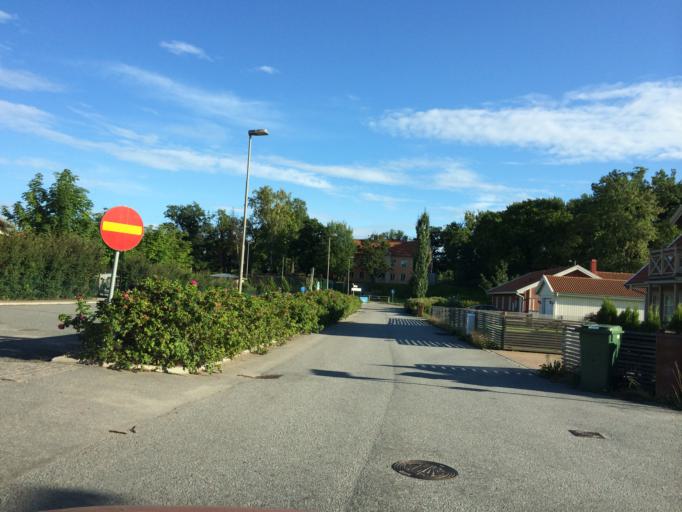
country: SE
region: Stockholm
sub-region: Huddinge Kommun
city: Segeltorp
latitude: 59.2739
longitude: 17.9277
